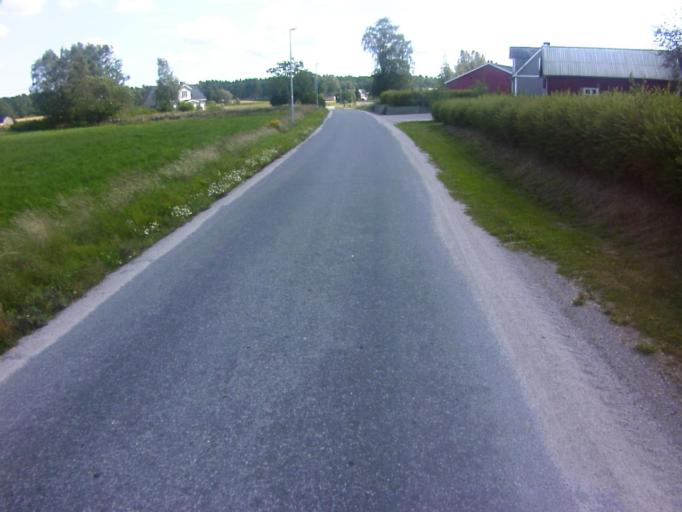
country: SE
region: Blekinge
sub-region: Olofstroms Kommun
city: Jamshog
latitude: 56.1959
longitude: 14.6107
